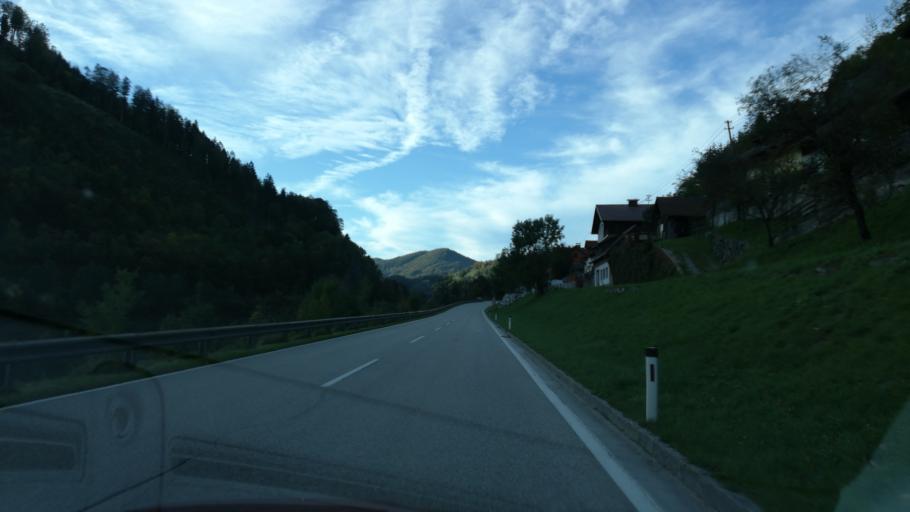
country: AT
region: Upper Austria
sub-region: Politischer Bezirk Steyr-Land
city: Losenstein
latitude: 47.9141
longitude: 14.4477
